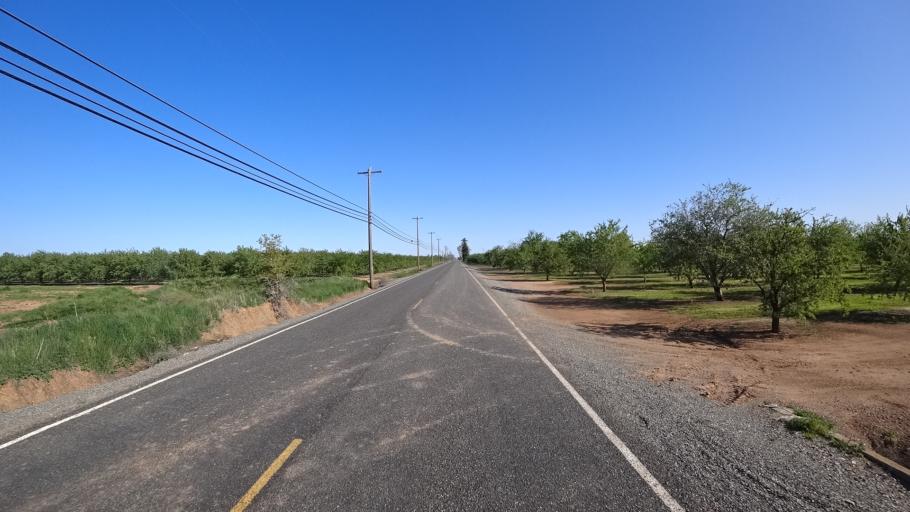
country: US
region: California
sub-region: Glenn County
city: Hamilton City
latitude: 39.7717
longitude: -122.1042
